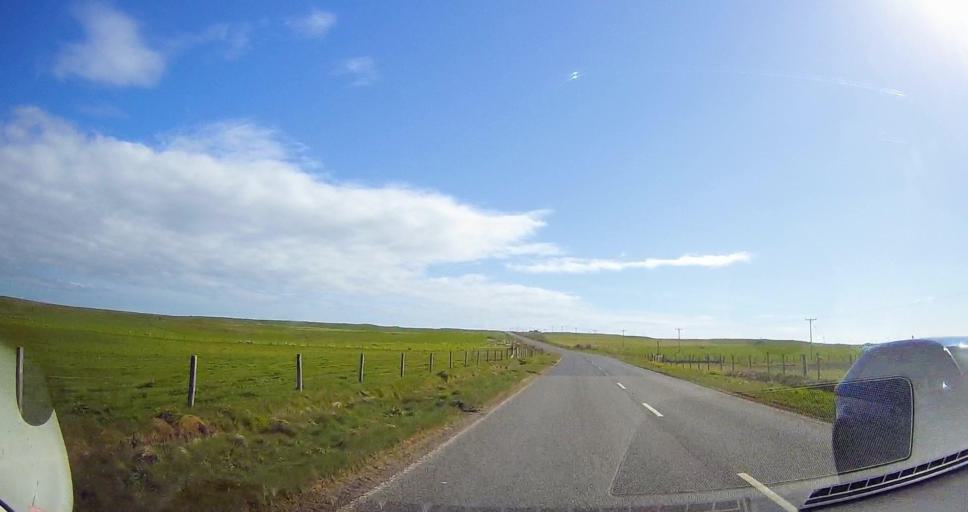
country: GB
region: Scotland
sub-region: Shetland Islands
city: Sandwick
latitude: 59.9086
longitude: -1.3011
